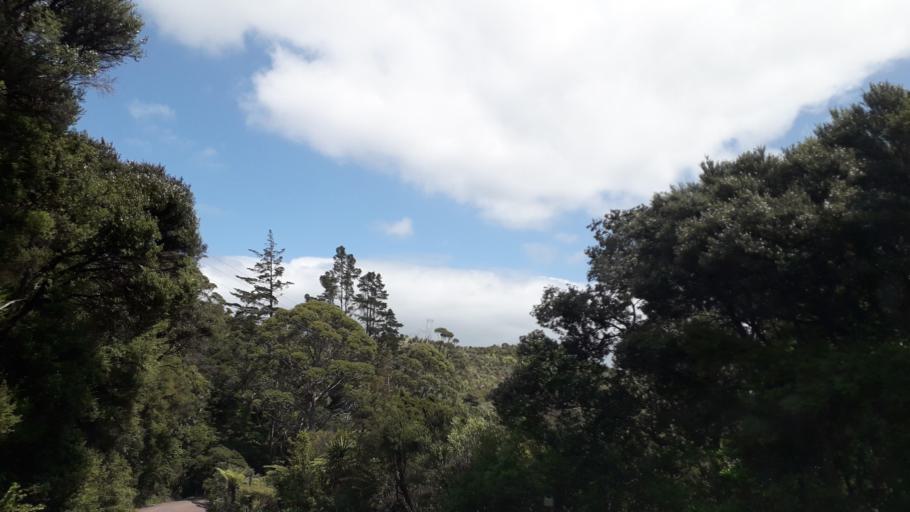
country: NZ
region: Northland
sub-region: Far North District
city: Paihia
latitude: -35.2378
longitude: 174.2556
